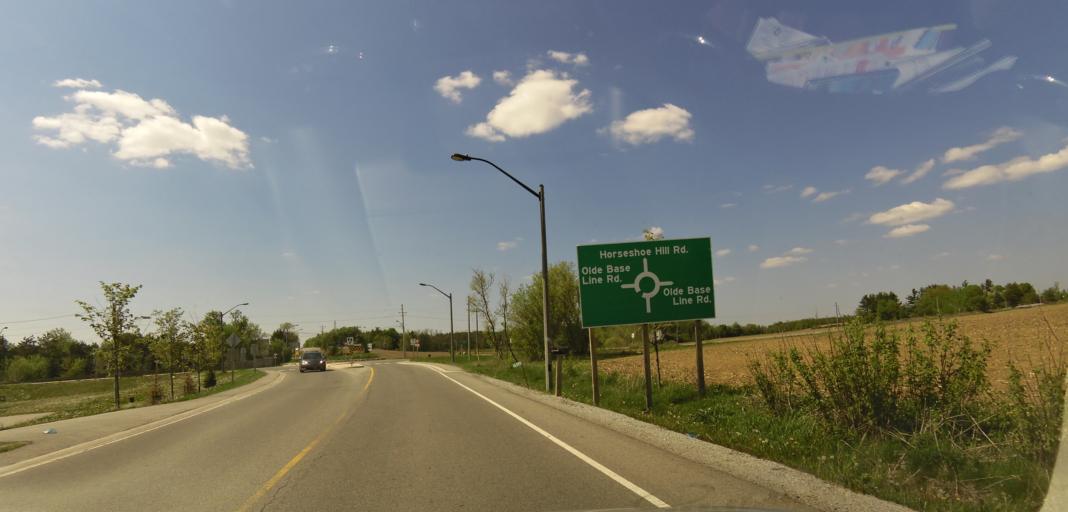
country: CA
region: Ontario
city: Brampton
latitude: 43.8291
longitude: -79.8822
